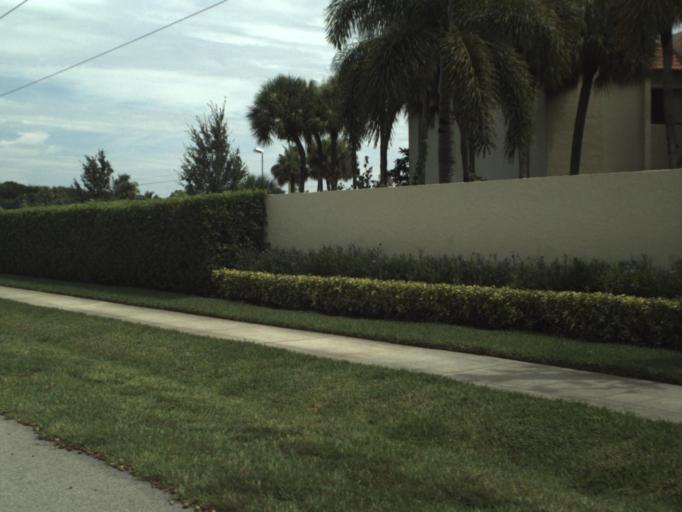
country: US
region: Florida
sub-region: Palm Beach County
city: Jupiter
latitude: 26.9205
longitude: -80.0739
